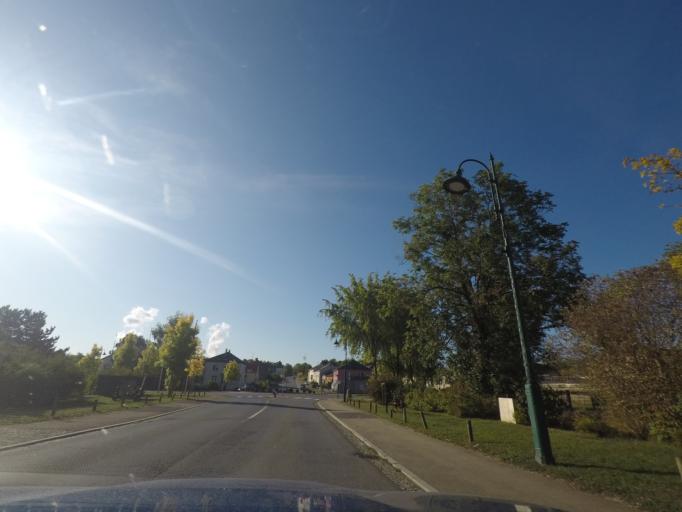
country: LU
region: Luxembourg
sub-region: Canton d'Esch-sur-Alzette
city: Frisange
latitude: 49.4584
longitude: 6.1780
